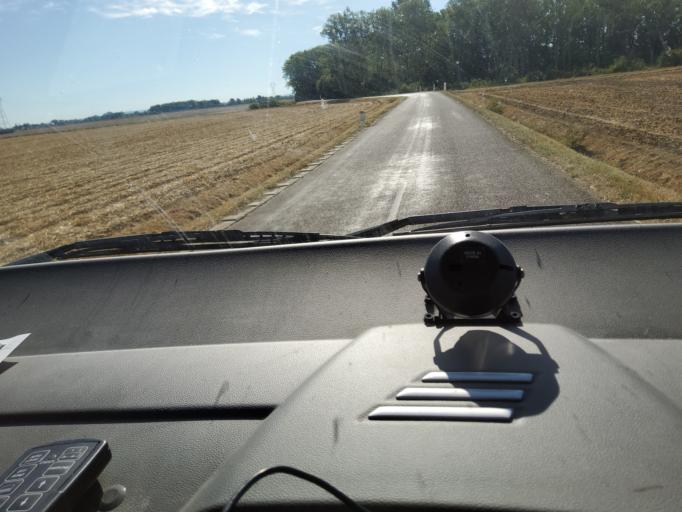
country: FR
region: Bourgogne
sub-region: Departement de la Cote-d'Or
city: Saint-Usage
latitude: 47.1400
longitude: 5.2539
